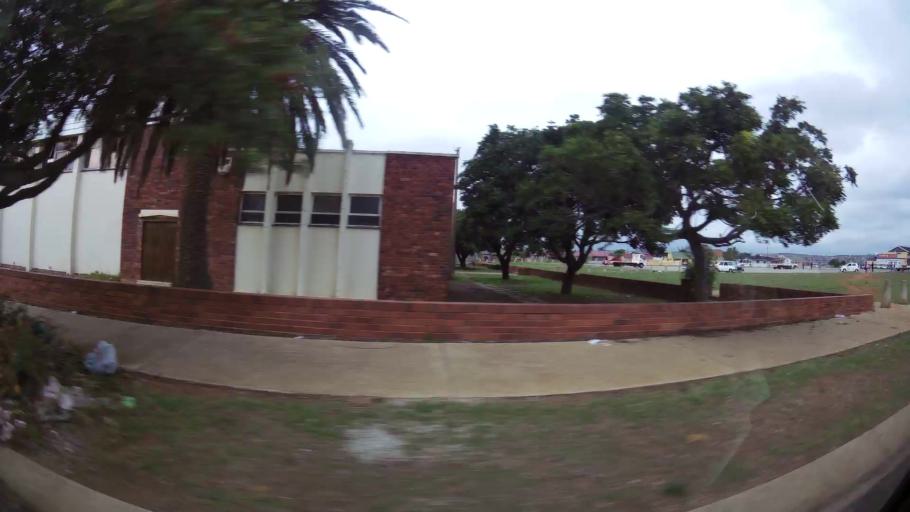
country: ZA
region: Eastern Cape
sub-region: Nelson Mandela Bay Metropolitan Municipality
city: Port Elizabeth
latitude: -33.9005
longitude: 25.5637
